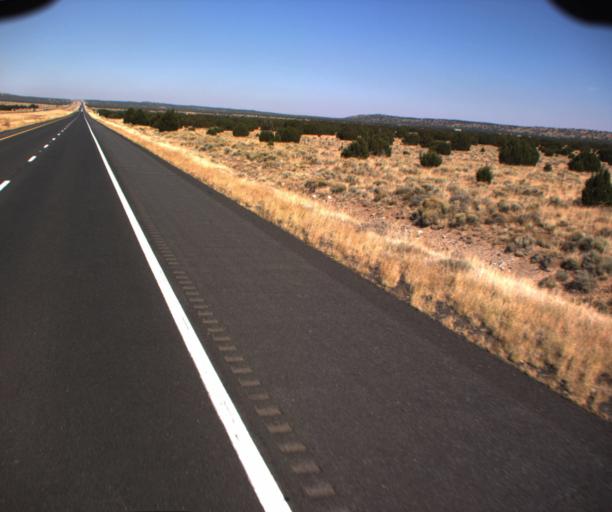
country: US
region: Arizona
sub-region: Coconino County
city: Flagstaff
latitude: 35.4334
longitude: -111.5673
